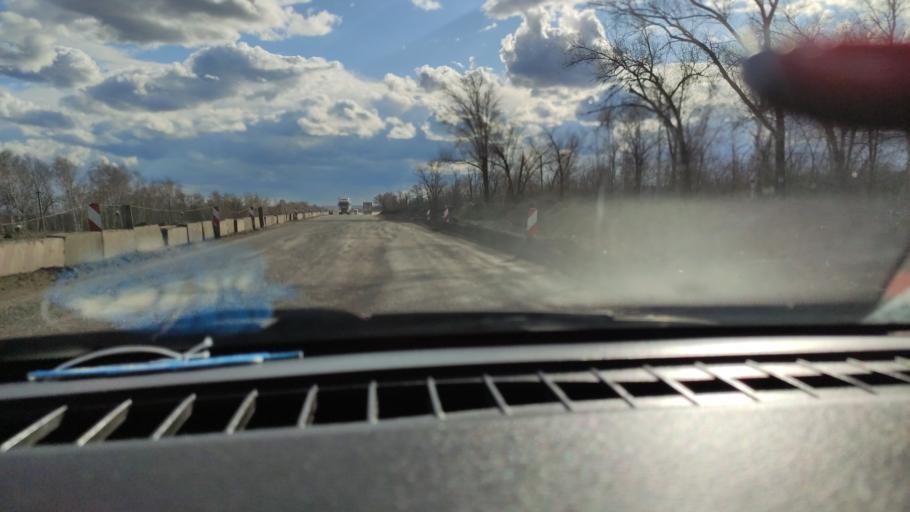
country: RU
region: Saratov
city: Sinodskoye
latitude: 52.0220
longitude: 46.7076
